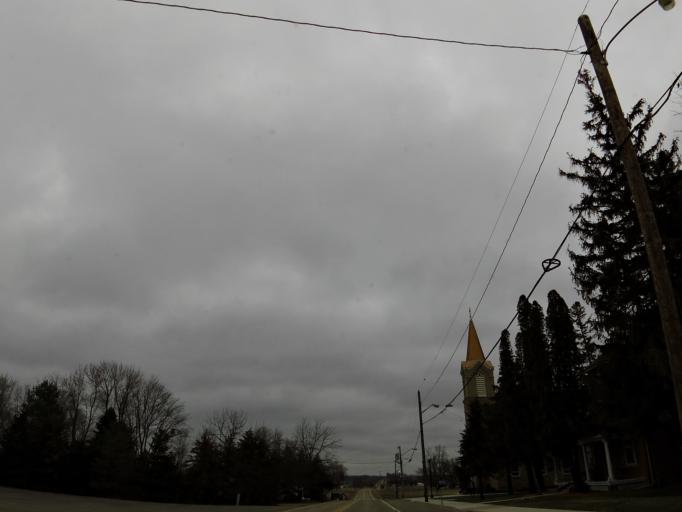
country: US
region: Minnesota
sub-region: Scott County
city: Shakopee
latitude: 44.7212
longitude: -93.5414
